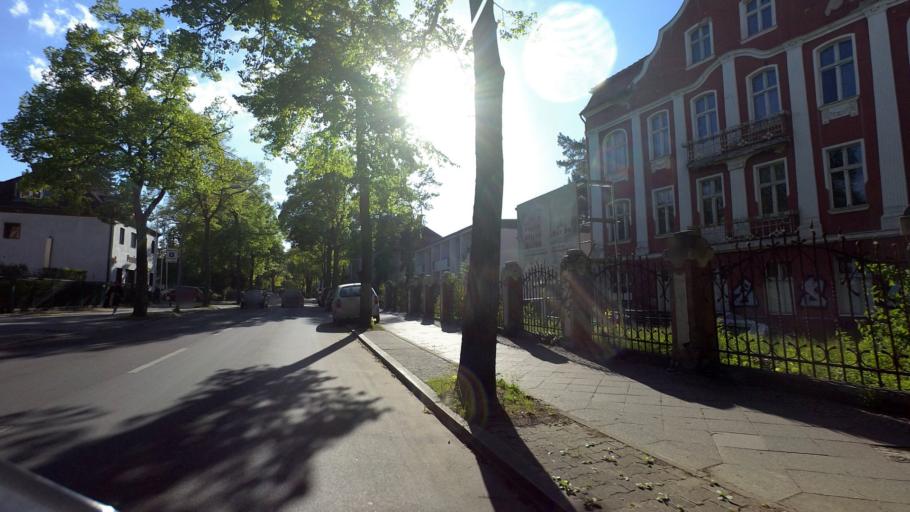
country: DE
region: Berlin
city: Waidmannslust
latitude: 52.6059
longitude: 13.3158
